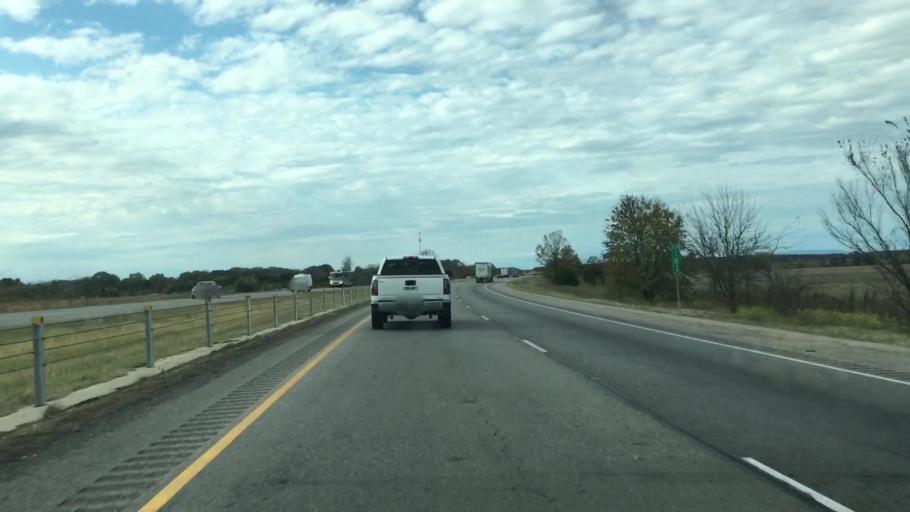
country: US
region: Arkansas
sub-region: Conway County
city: Morrilton
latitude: 35.1962
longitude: -92.8002
